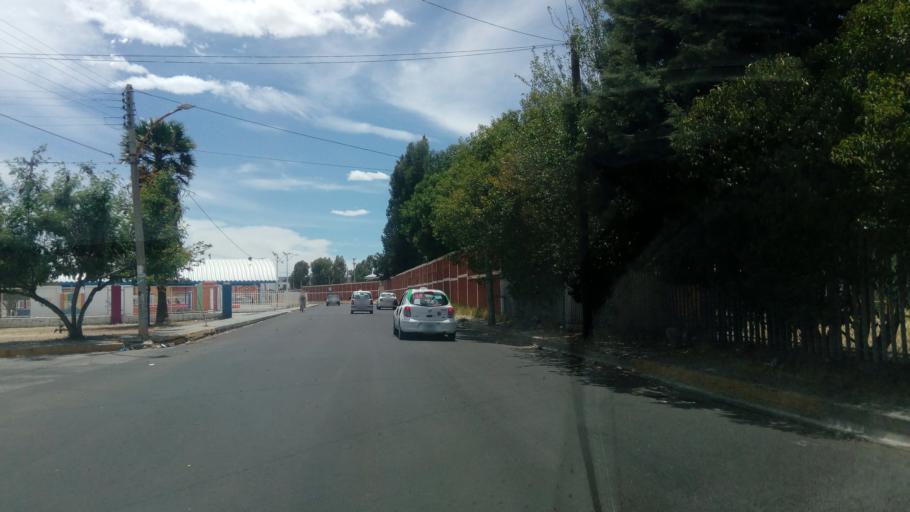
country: MX
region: Durango
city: Victoria de Durango
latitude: 24.0097
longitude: -104.6737
